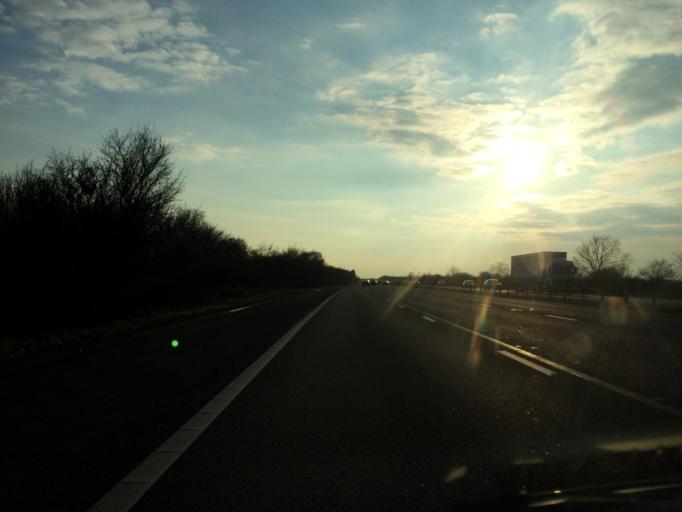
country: GB
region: England
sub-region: Wiltshire
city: Lyneham
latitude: 51.5373
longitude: -1.9929
